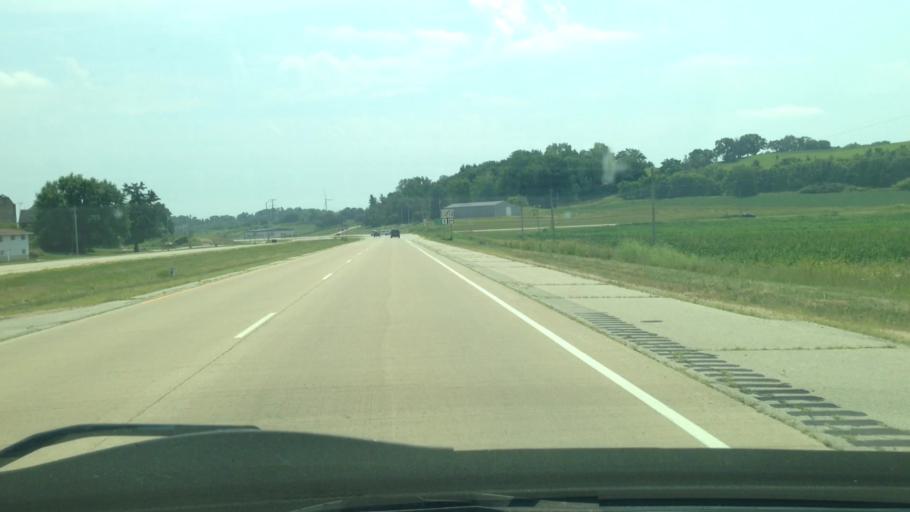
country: US
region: Wisconsin
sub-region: Dane County
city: Cross Plains
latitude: 43.1981
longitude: -89.5841
